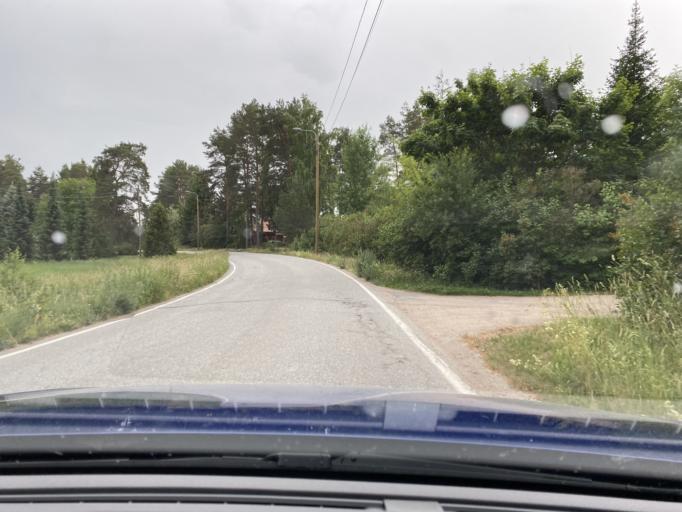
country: FI
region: Satakunta
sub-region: Rauma
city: Eura
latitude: 61.1521
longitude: 22.1199
